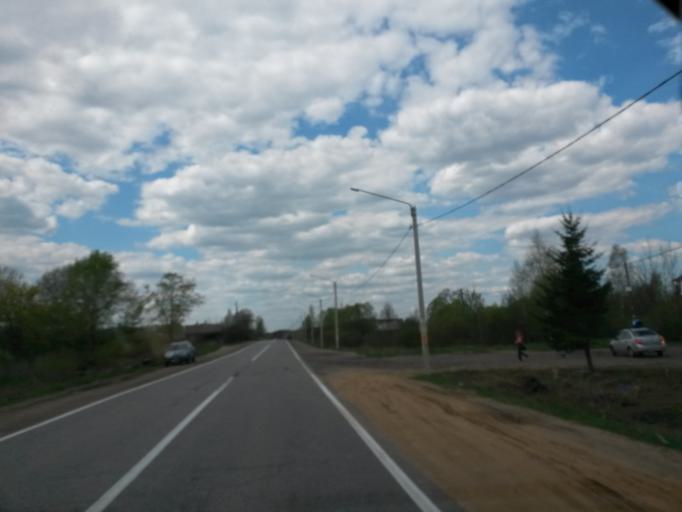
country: RU
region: Jaroslavl
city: Kurba
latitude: 57.6784
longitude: 39.5766
